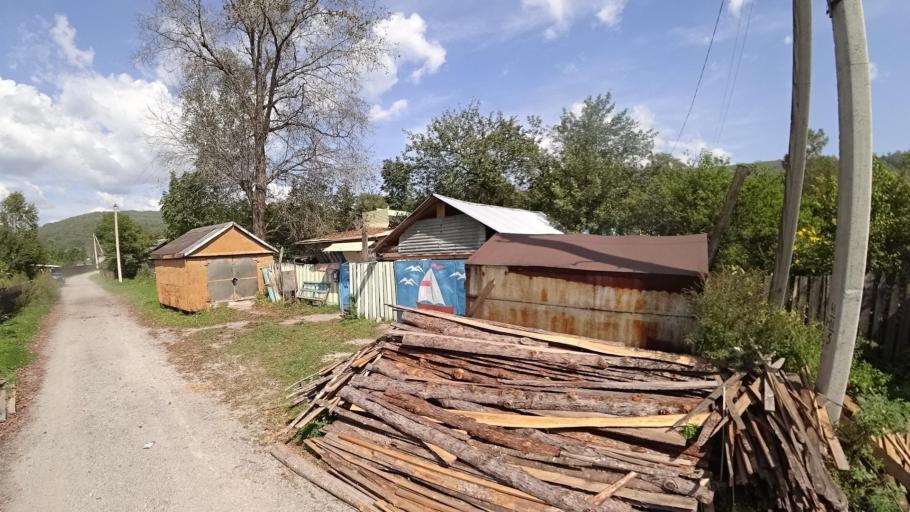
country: RU
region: Jewish Autonomous Oblast
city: Londoko
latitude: 49.0243
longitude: 131.9327
